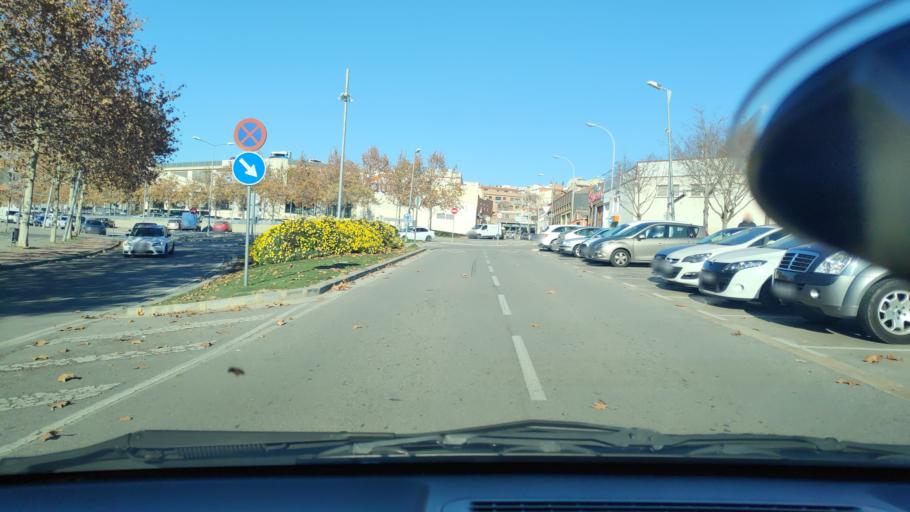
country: ES
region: Catalonia
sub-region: Provincia de Barcelona
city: Sant Quirze del Valles
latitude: 41.5448
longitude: 2.0920
